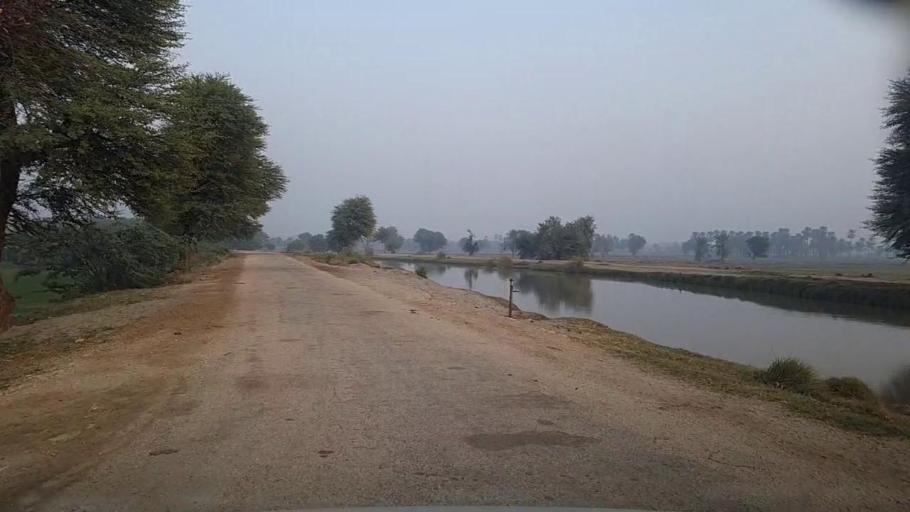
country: PK
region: Sindh
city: Kandiari
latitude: 27.0317
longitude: 68.5652
